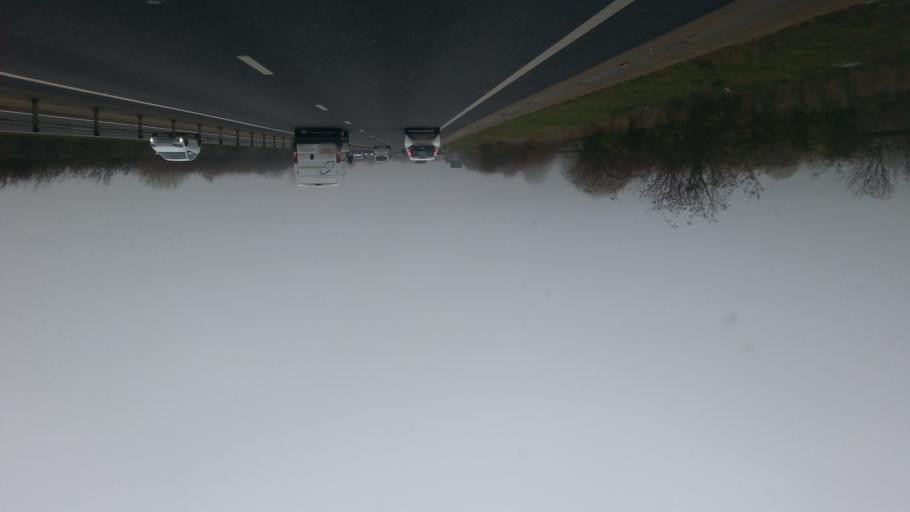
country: GB
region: England
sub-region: Cambridgeshire
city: Papworth Everard
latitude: 52.2287
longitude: -0.0871
